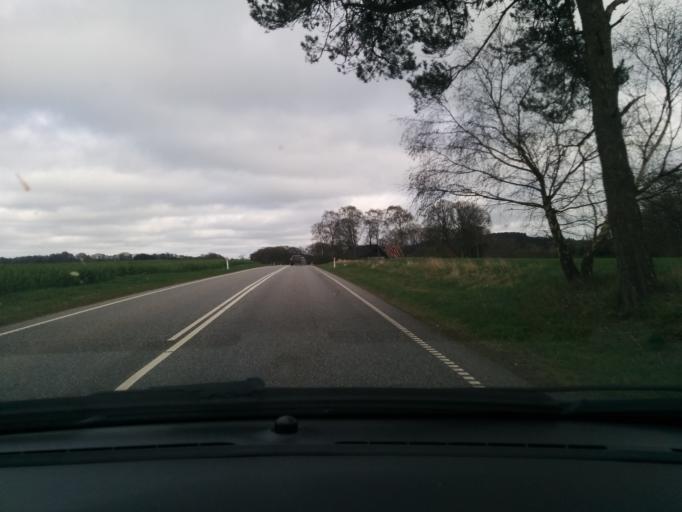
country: DK
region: Central Jutland
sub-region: Favrskov Kommune
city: Hammel
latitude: 56.2114
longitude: 9.7763
